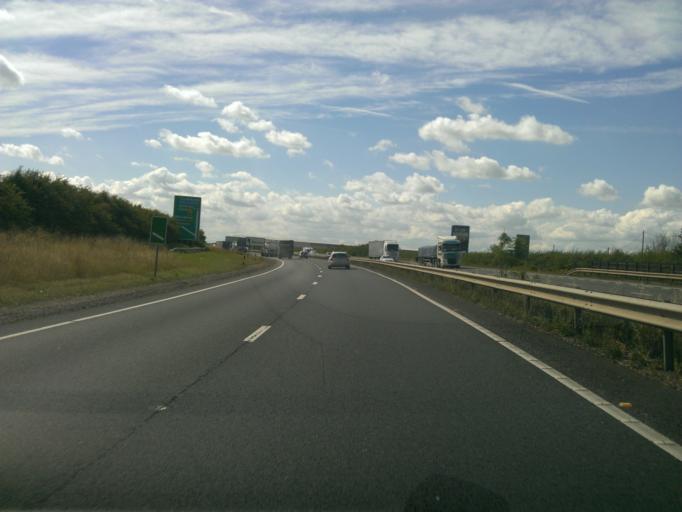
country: GB
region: England
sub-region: Northamptonshire
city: Thrapston
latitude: 52.3923
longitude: -0.5146
